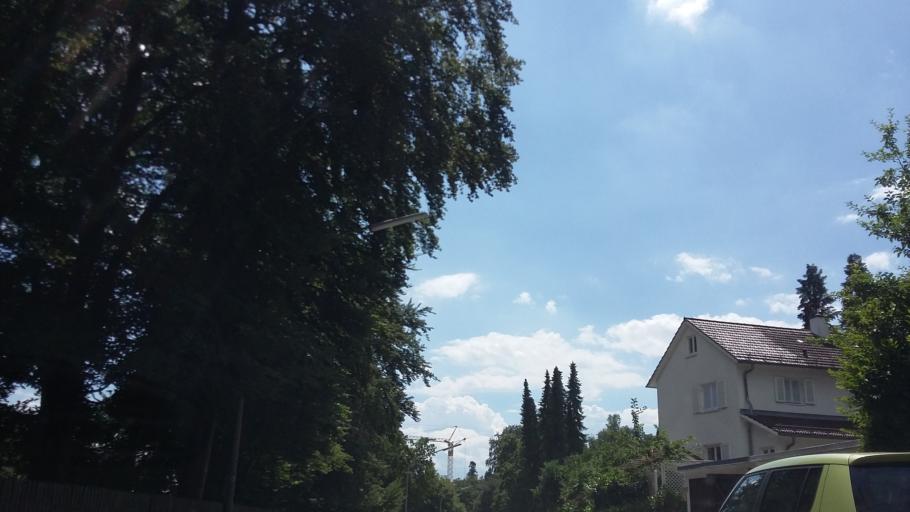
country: DE
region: Bavaria
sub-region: Upper Bavaria
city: Starnberg
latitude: 48.0106
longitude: 11.3436
